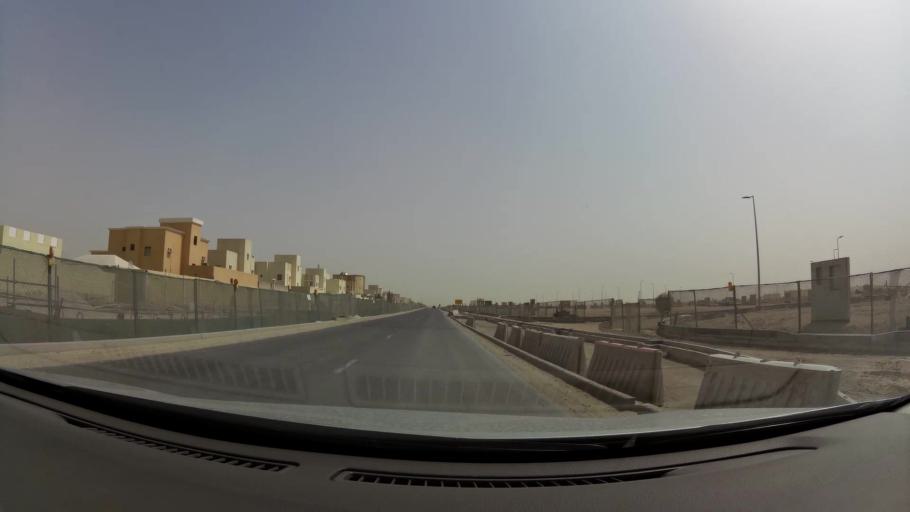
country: QA
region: Baladiyat ar Rayyan
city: Ar Rayyan
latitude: 25.2495
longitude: 51.3610
